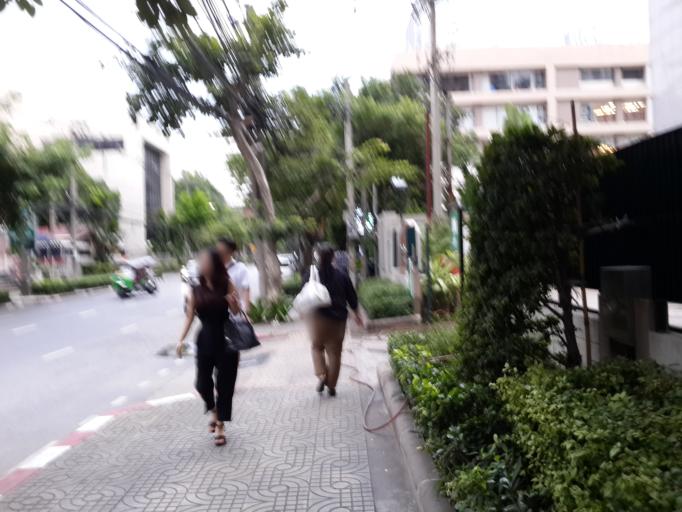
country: TH
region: Bangkok
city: Pathum Wan
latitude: 13.7413
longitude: 100.5435
